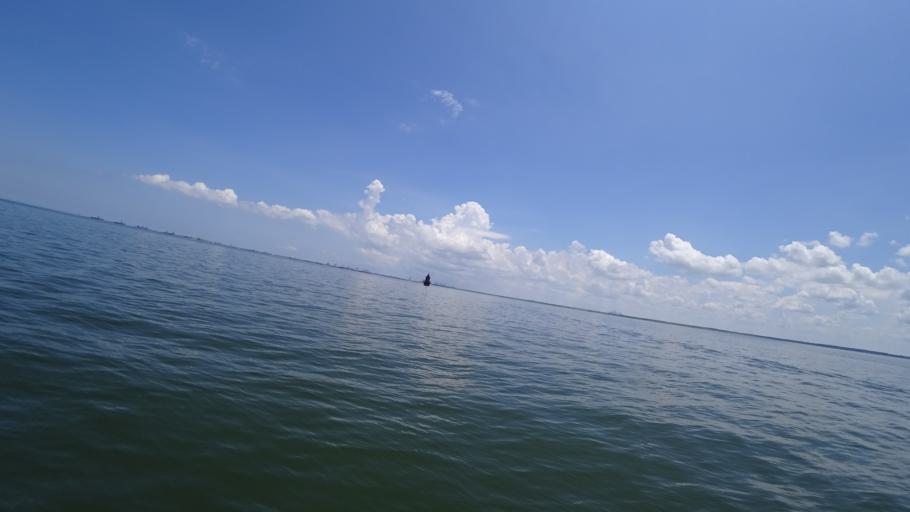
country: US
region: Virginia
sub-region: City of Newport News
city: Newport News
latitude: 36.9477
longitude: -76.3962
